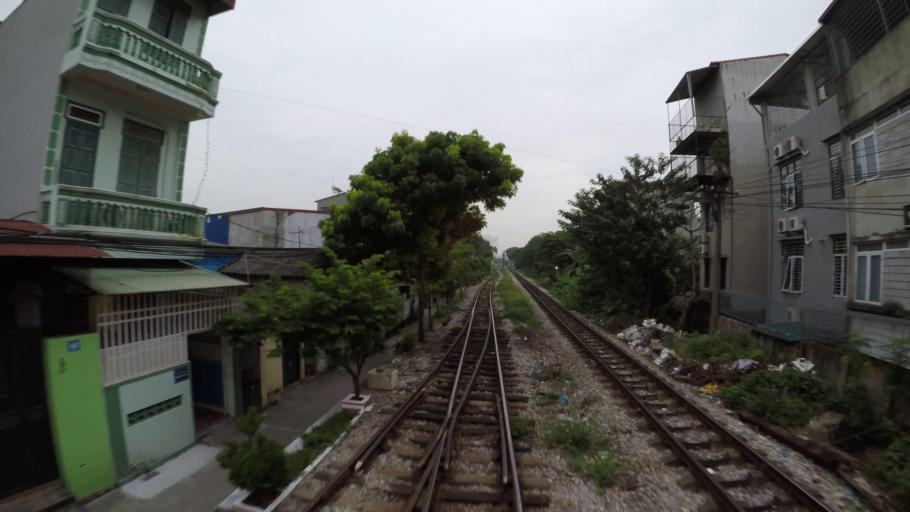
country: VN
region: Ha Noi
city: Trau Quy
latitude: 21.0368
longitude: 105.8996
